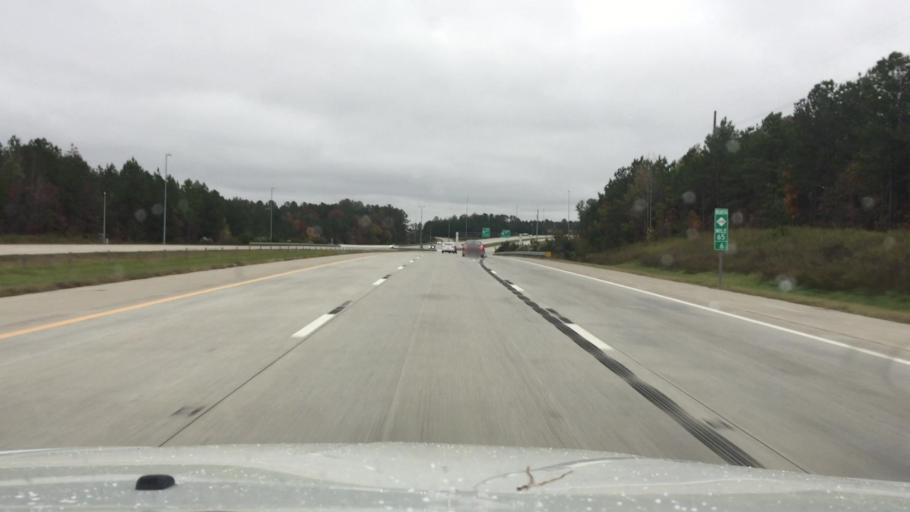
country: US
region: North Carolina
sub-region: Wake County
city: Green Level
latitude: 35.8331
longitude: -78.8914
